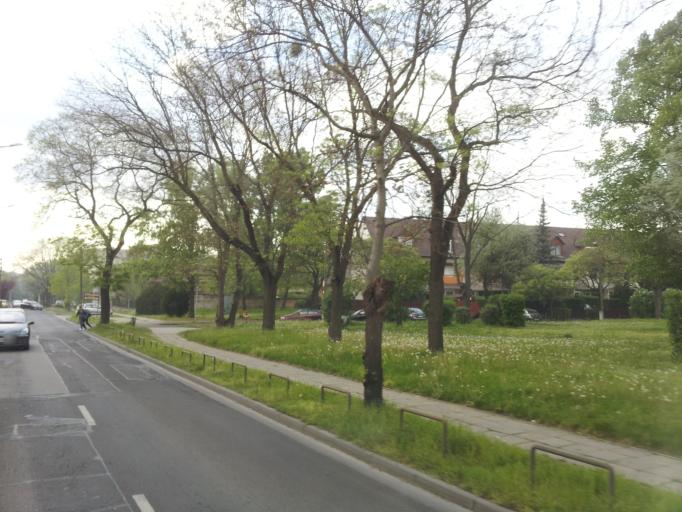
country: HU
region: Budapest
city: Budapest XV. keruelet
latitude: 47.5723
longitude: 19.1244
